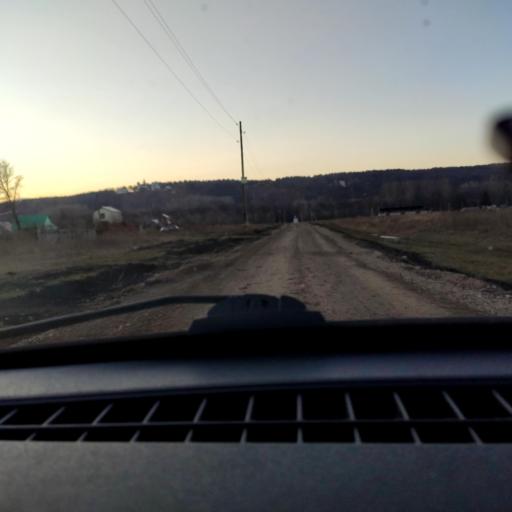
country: RU
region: Bashkortostan
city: Ufa
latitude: 54.7365
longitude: 56.0496
